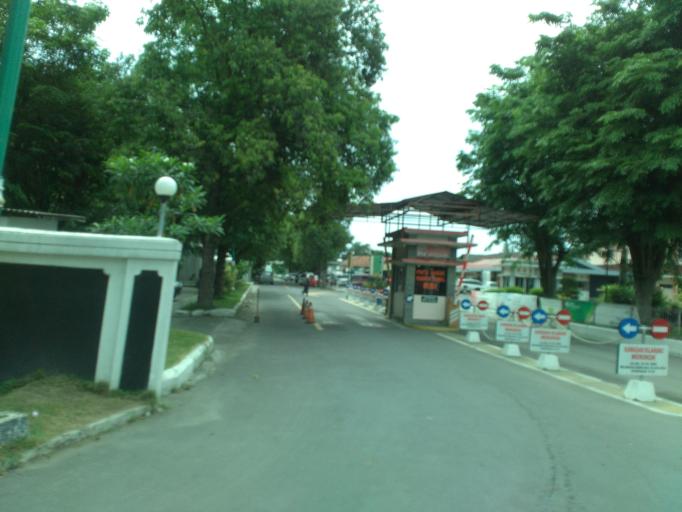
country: ID
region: Central Java
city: Klaten
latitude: -7.6864
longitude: 110.6348
